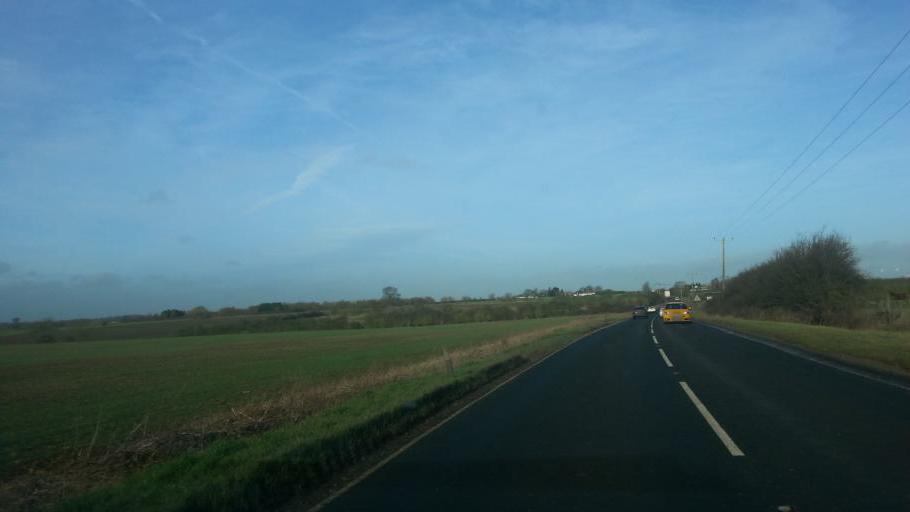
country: GB
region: England
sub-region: Cambridgeshire
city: Warboys
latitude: 52.4095
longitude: -0.1011
